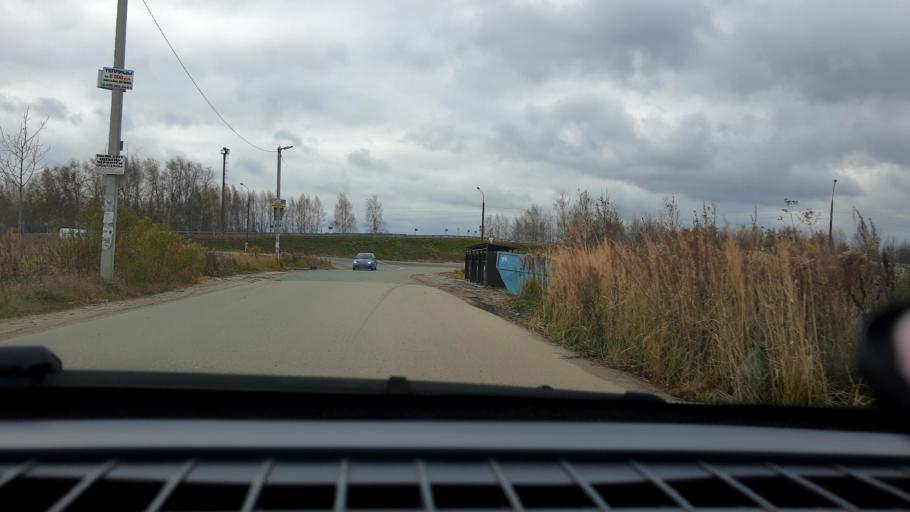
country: RU
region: Nizjnij Novgorod
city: Afonino
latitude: 56.1978
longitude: 44.1245
